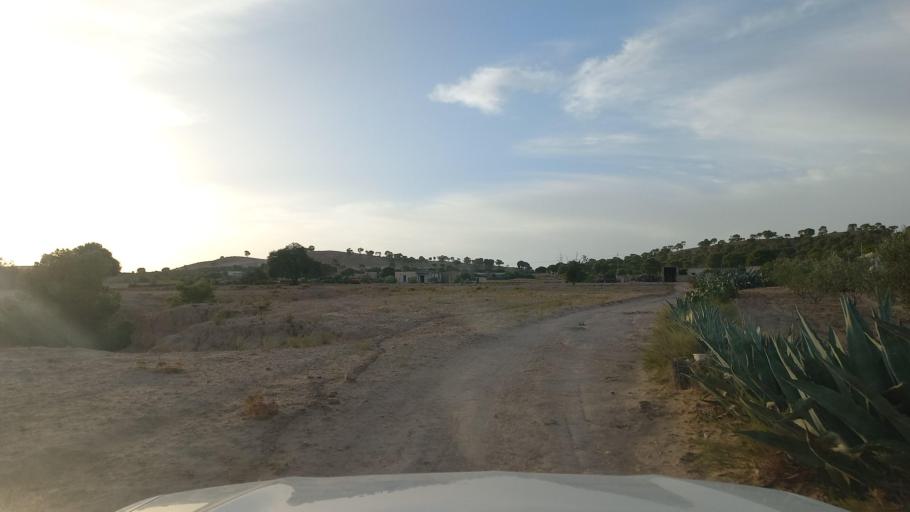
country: TN
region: Al Qasrayn
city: Sbiba
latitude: 35.4117
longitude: 8.9146
